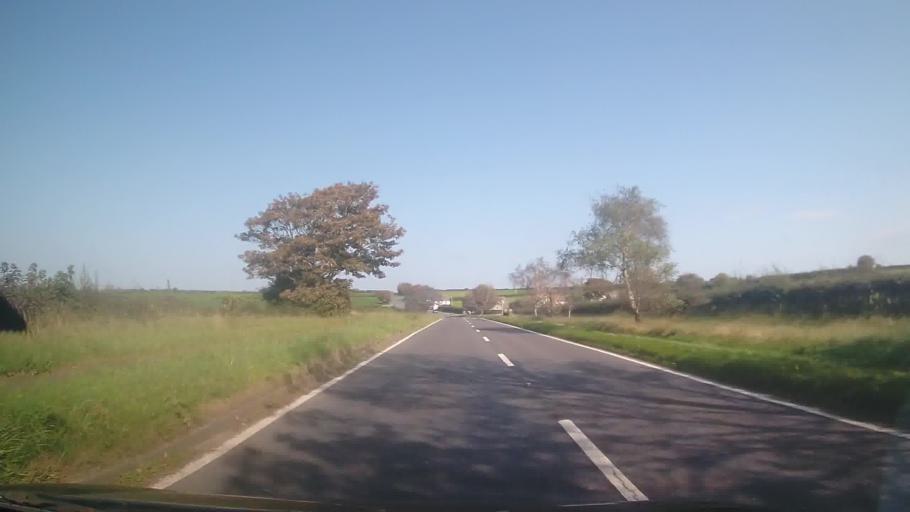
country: GB
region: Wales
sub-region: County of Ceredigion
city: Cardigan
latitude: 52.1019
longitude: -4.6073
